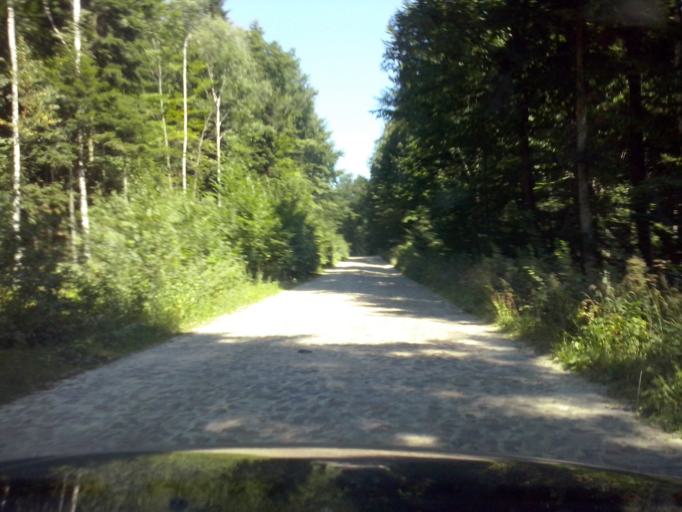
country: PL
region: Swietokrzyskie
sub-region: Powiat kielecki
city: Bieliny
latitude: 50.7859
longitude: 20.9310
